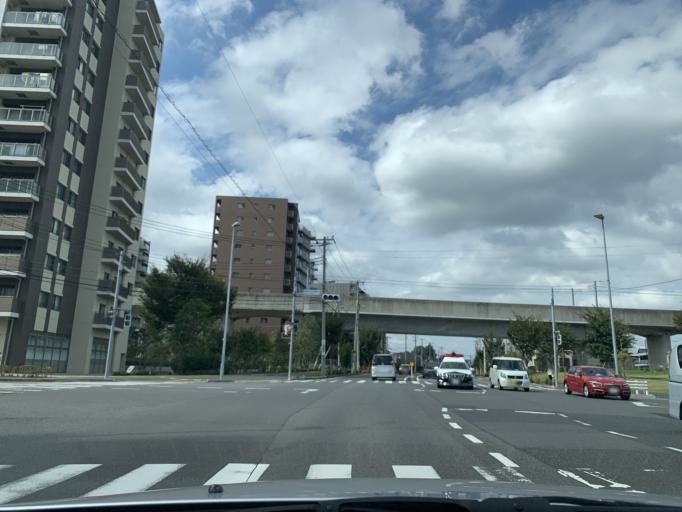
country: JP
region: Chiba
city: Nagareyama
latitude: 35.8742
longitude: 139.9290
